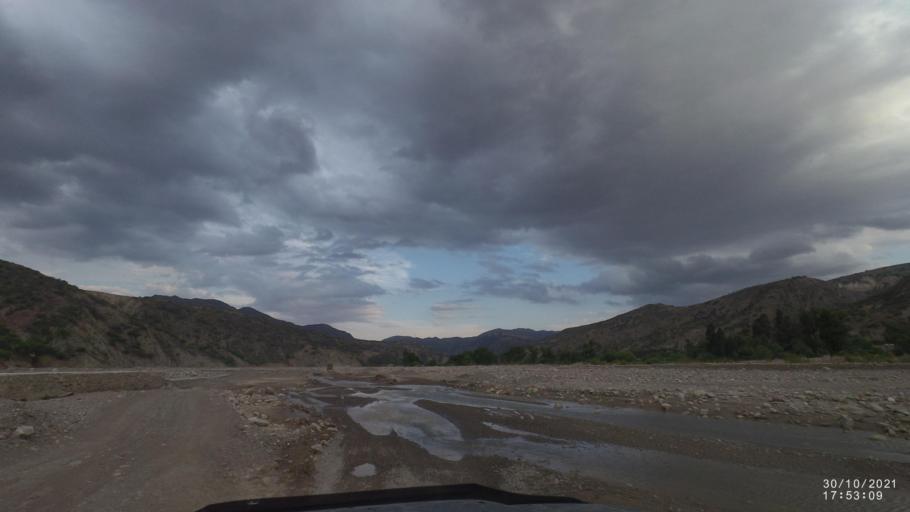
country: BO
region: Cochabamba
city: Sipe Sipe
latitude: -17.5391
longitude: -66.4959
